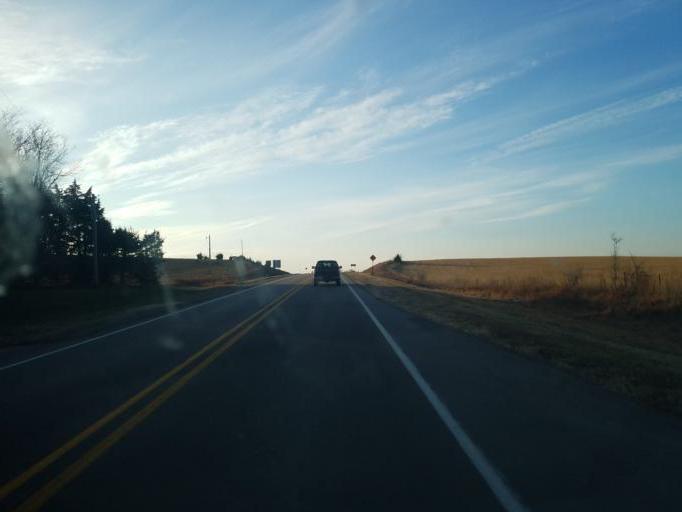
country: US
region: South Dakota
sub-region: Yankton County
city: Yankton
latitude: 42.7286
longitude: -97.4096
